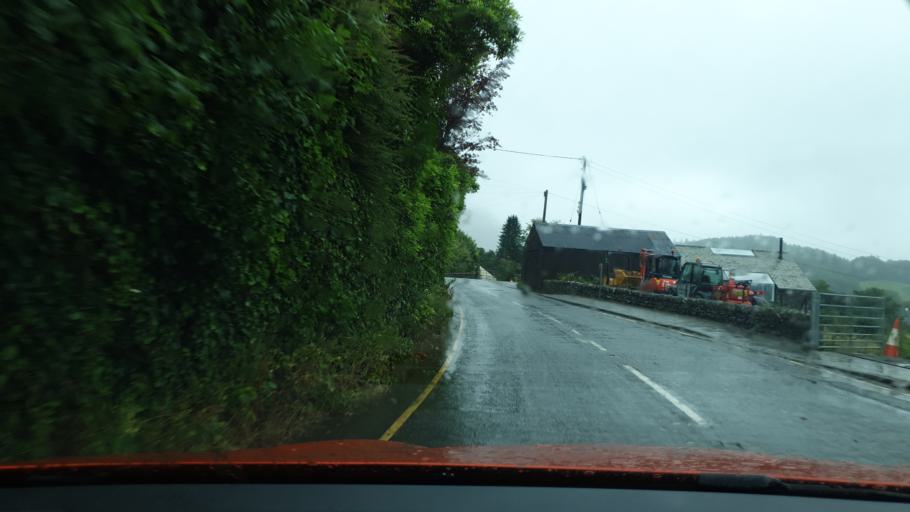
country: GB
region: England
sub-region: Cumbria
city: Ambleside
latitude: 54.3653
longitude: -3.0768
